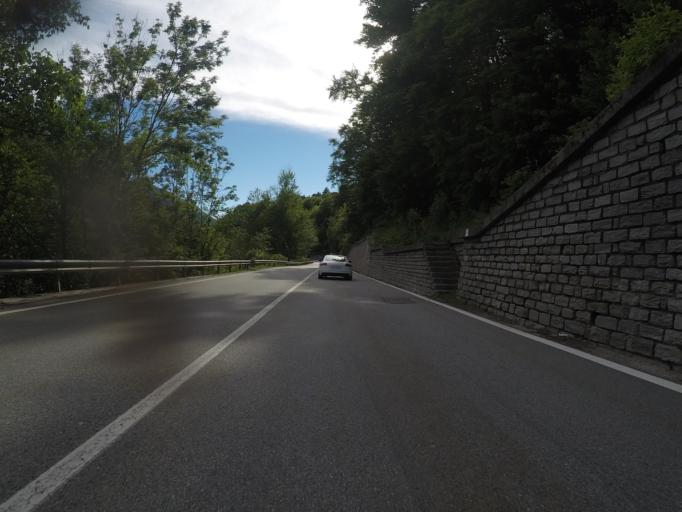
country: IT
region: Piedmont
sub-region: Provincia Verbano-Cusio-Ossola
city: Druogno
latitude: 46.1302
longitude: 8.3994
